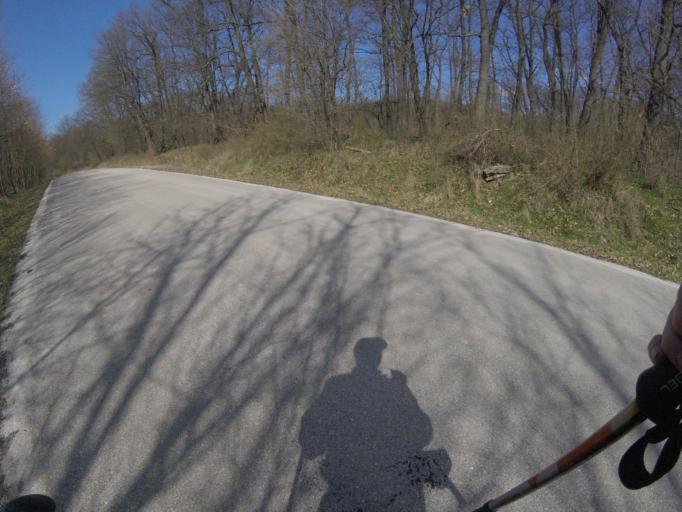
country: HU
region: Fejer
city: Pusztavam
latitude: 47.4327
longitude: 18.2862
